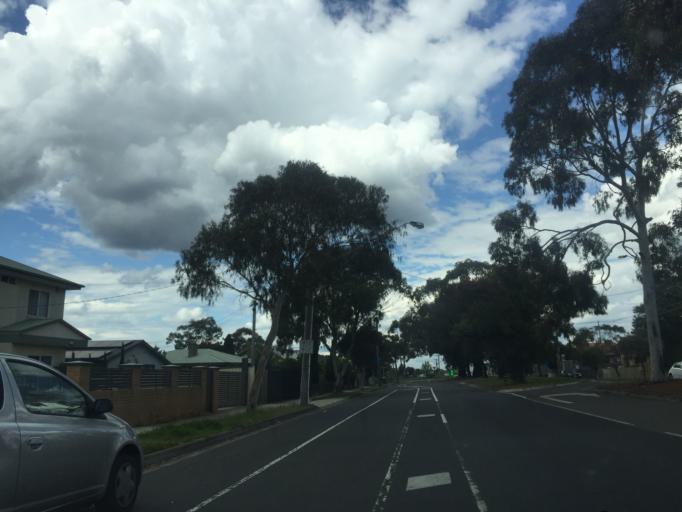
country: AU
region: Victoria
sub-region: Darebin
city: Kingsbury
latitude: -37.7181
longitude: 145.0195
